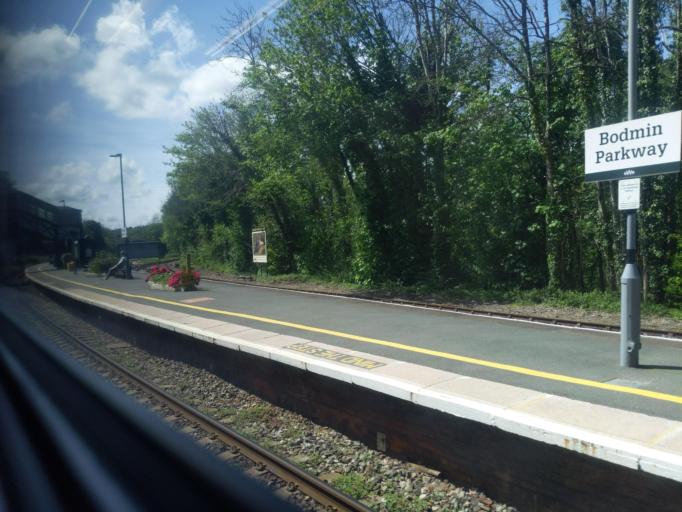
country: GB
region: England
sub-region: Cornwall
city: Lostwithiel
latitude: 50.4462
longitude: -4.6620
